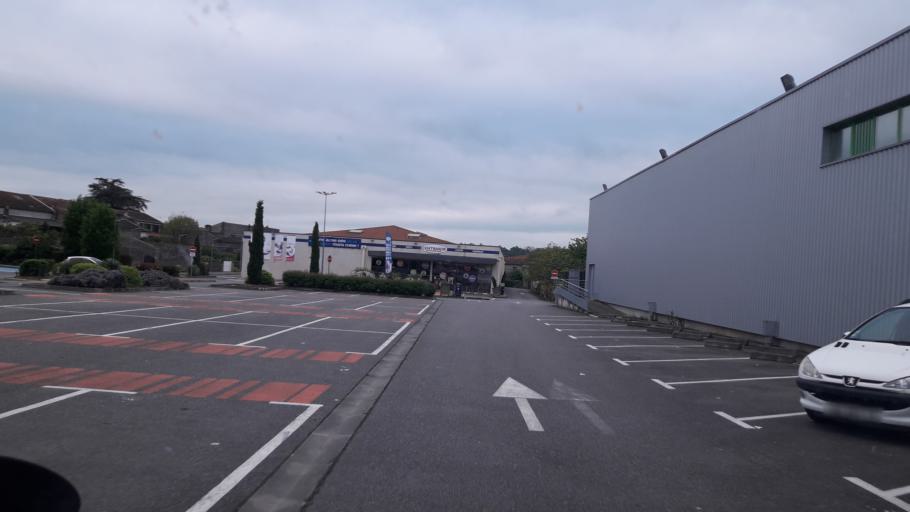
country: FR
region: Midi-Pyrenees
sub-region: Departement de la Haute-Garonne
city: Cazeres
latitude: 43.2099
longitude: 1.0842
